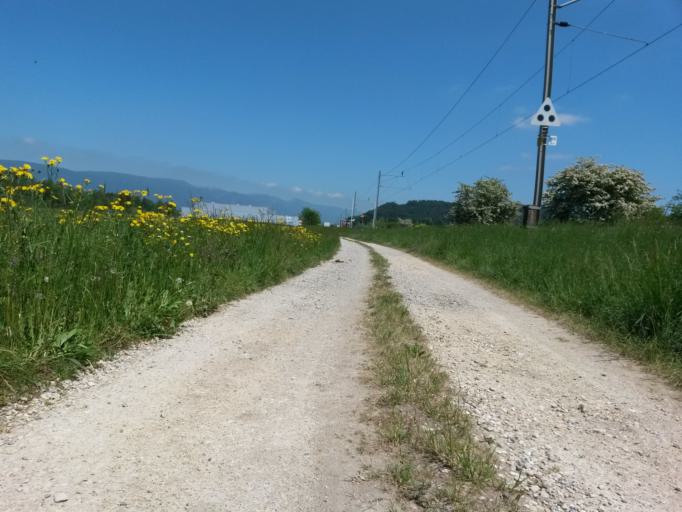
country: CH
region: Bern
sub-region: Seeland District
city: Worben
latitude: 47.1110
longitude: 7.3294
